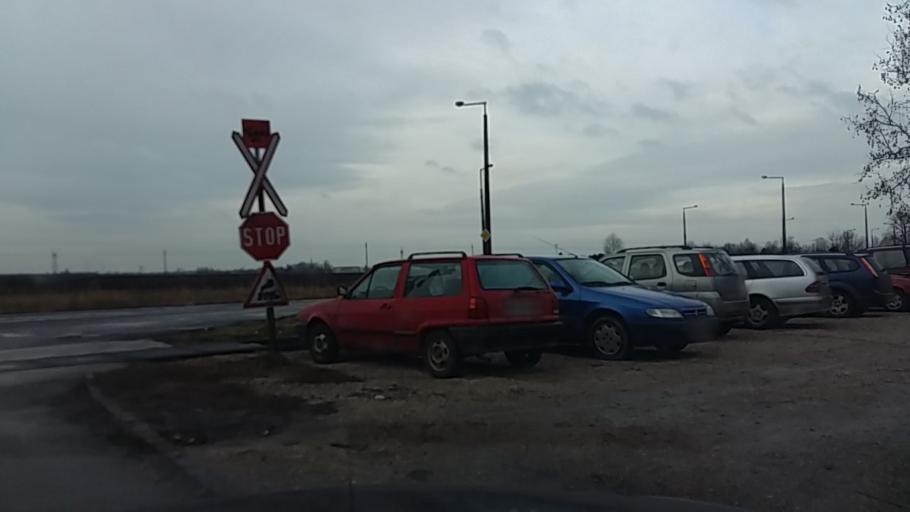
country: HU
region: Fejer
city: Pusztaszabolcs
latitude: 47.0825
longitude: 18.7175
